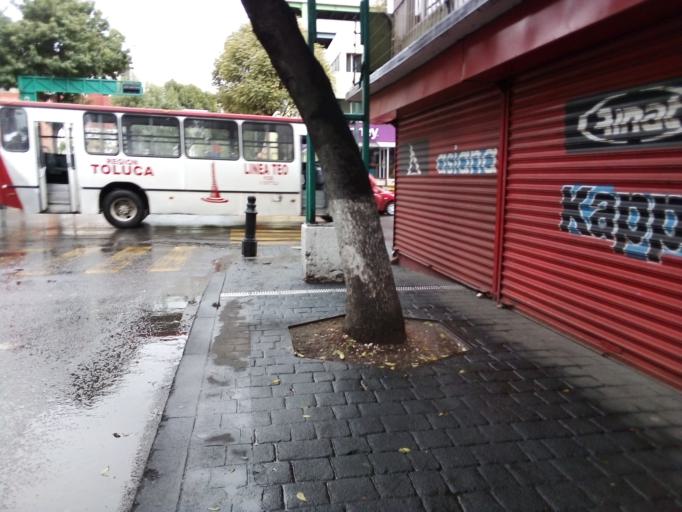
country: MX
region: Mexico
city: Toluca
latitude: 19.2879
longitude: -99.6584
